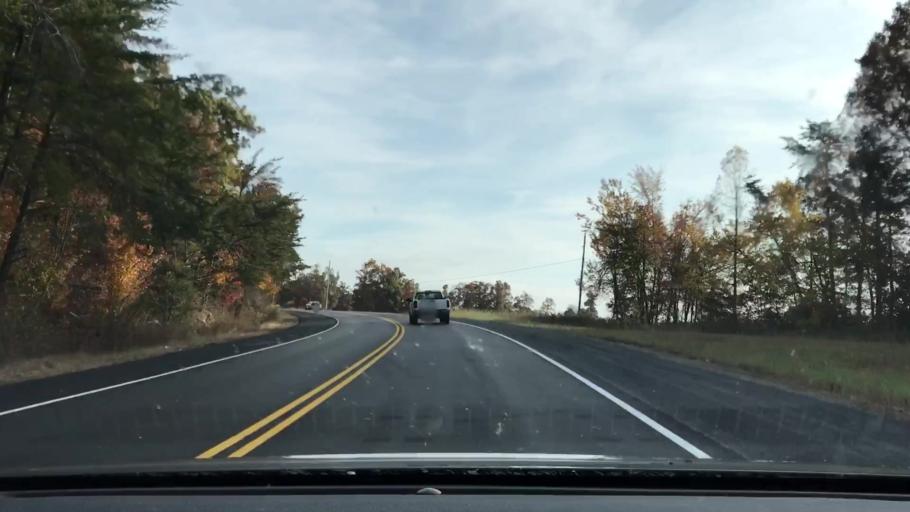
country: US
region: Tennessee
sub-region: Putnam County
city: Monterey
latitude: 36.1350
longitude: -85.1079
